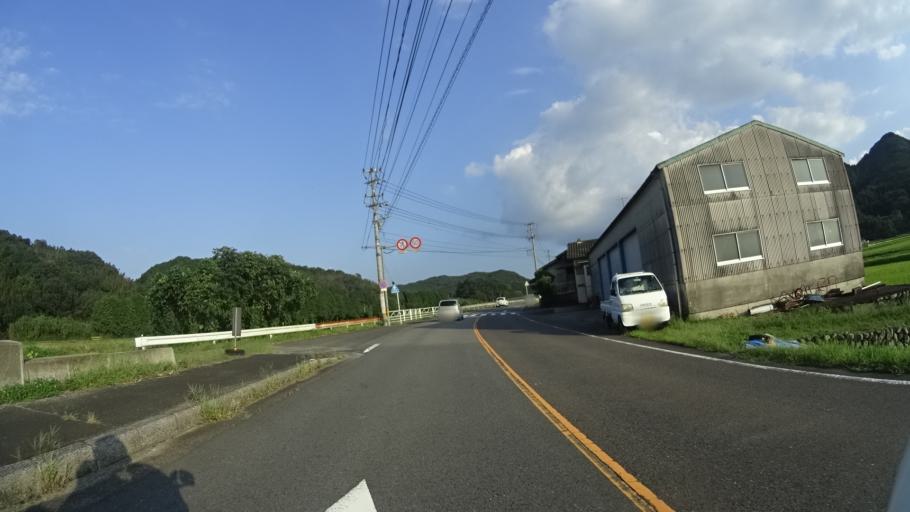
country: JP
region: Oita
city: Bungo-Takada-shi
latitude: 33.4347
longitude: 131.3689
